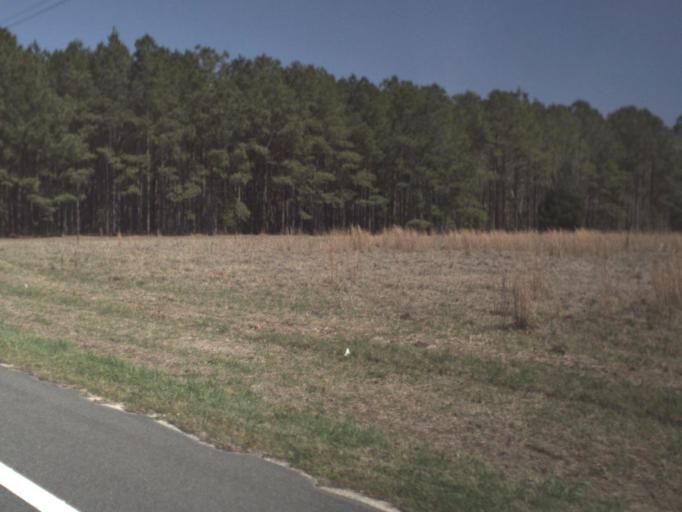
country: US
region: Florida
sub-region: Gadsden County
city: Quincy
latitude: 30.5146
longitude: -84.6090
